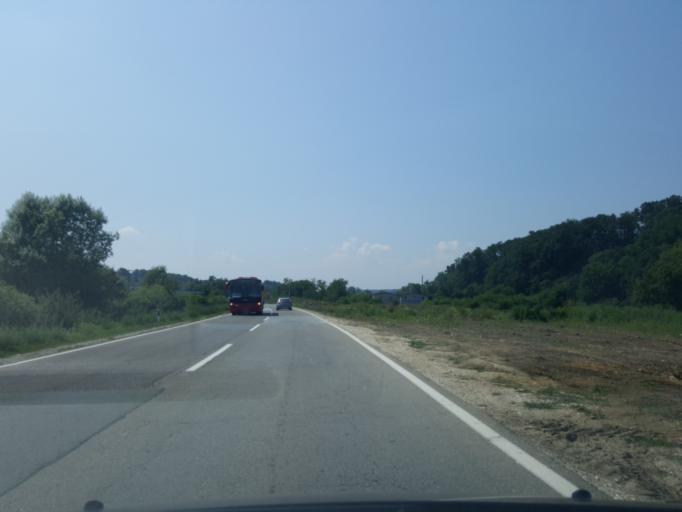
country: RS
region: Central Serbia
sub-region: Belgrade
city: Mladenovac
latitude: 44.4993
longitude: 20.6558
